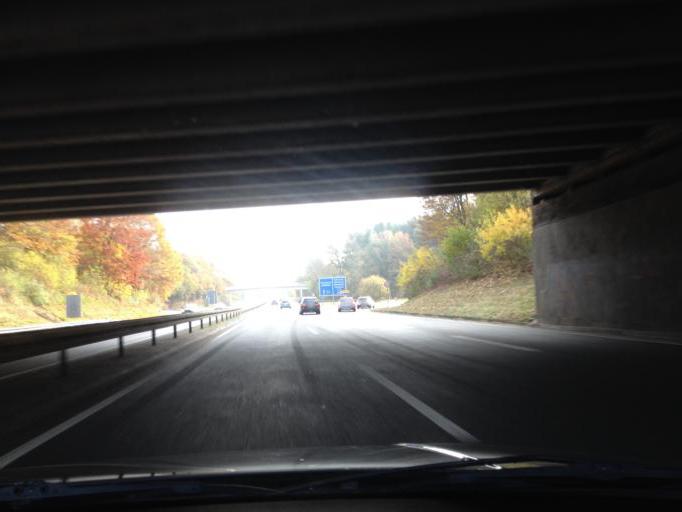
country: DE
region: Saarland
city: Kirkel
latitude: 49.3098
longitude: 7.2541
